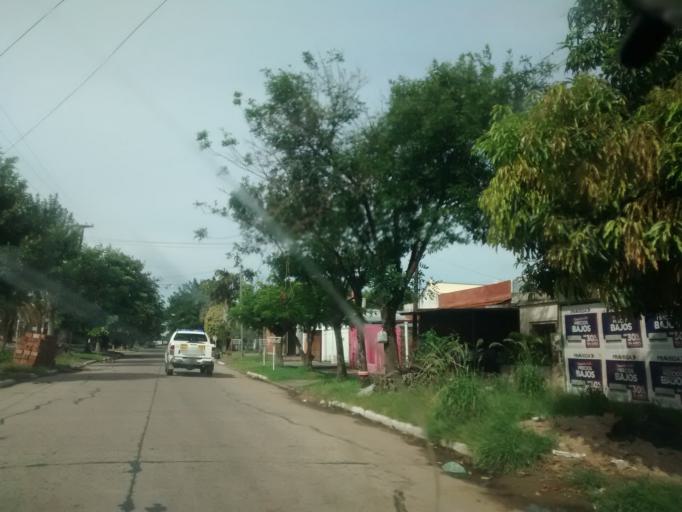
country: AR
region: Chaco
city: Resistencia
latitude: -27.4398
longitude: -58.9954
